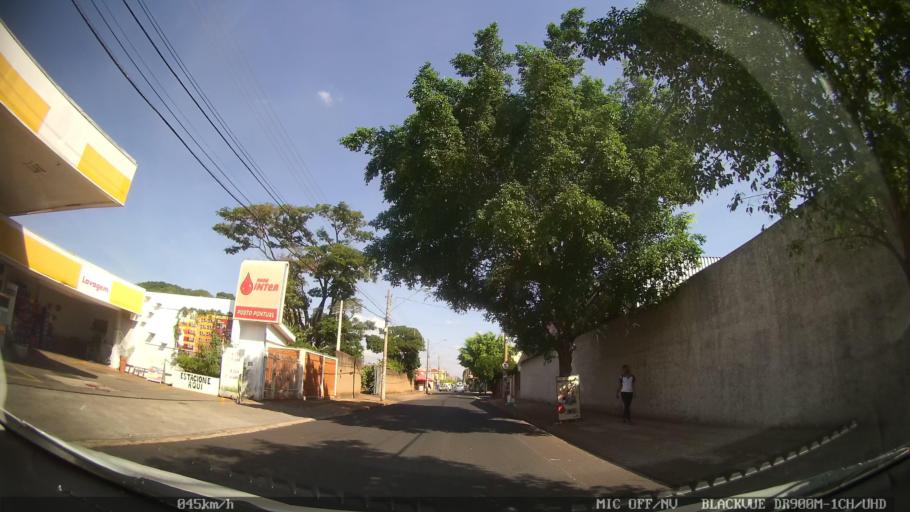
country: BR
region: Sao Paulo
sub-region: Ribeirao Preto
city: Ribeirao Preto
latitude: -21.1798
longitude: -47.8235
